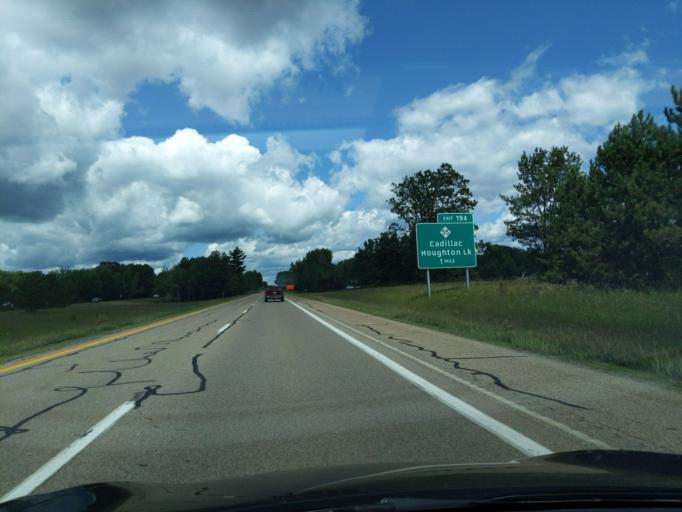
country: US
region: Michigan
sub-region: Roscommon County
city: Houghton Lake
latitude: 44.3148
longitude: -84.8058
